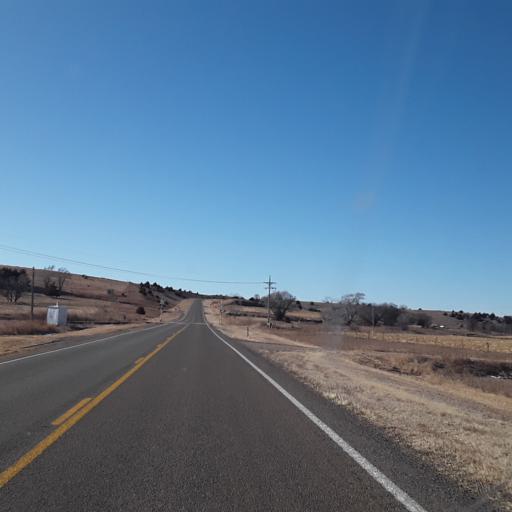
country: US
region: Nebraska
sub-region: Frontier County
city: Stockville
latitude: 40.6326
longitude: -100.5728
